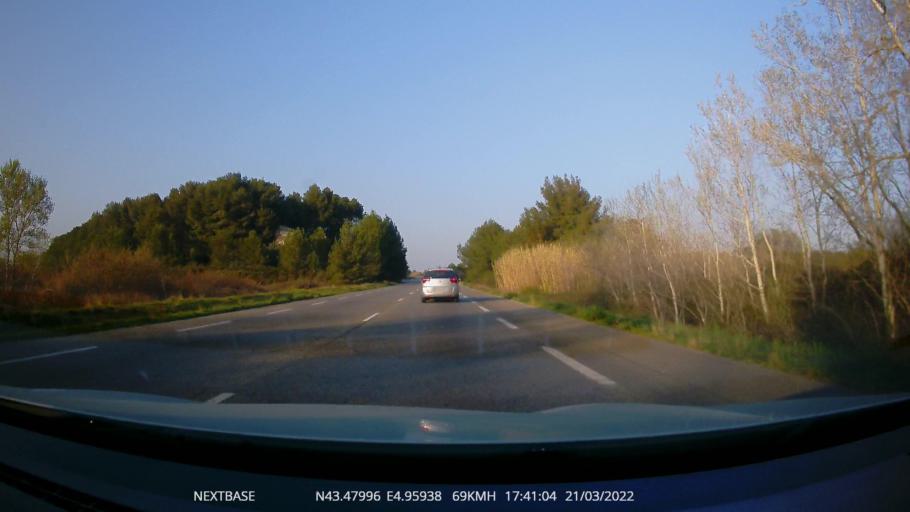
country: FR
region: Provence-Alpes-Cote d'Azur
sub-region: Departement des Bouches-du-Rhone
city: Istres
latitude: 43.4800
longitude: 4.9594
